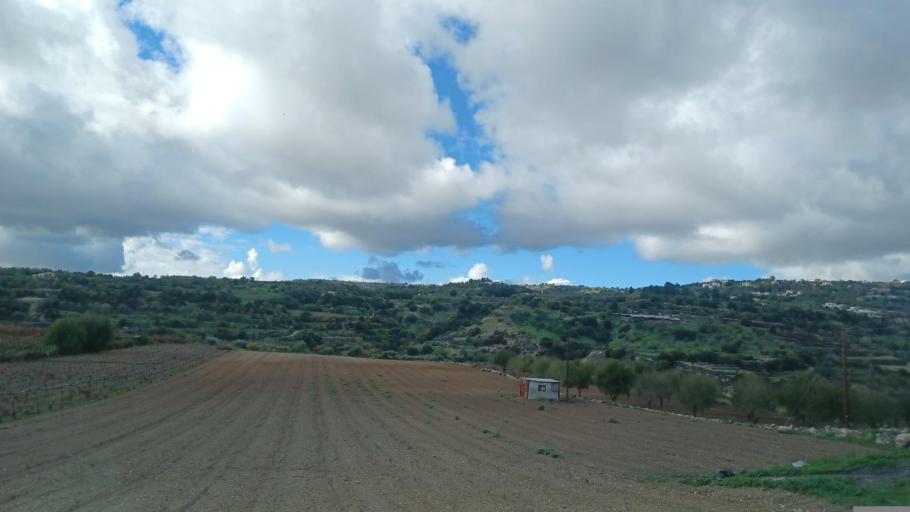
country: CY
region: Pafos
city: Mesogi
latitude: 34.8473
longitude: 32.5156
